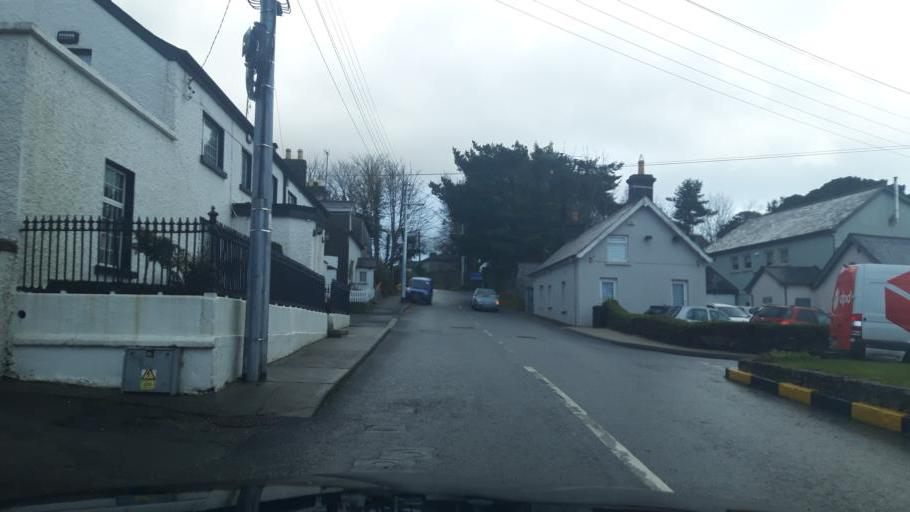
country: IE
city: Newtownmountkennedy
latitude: 53.0928
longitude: -6.1123
